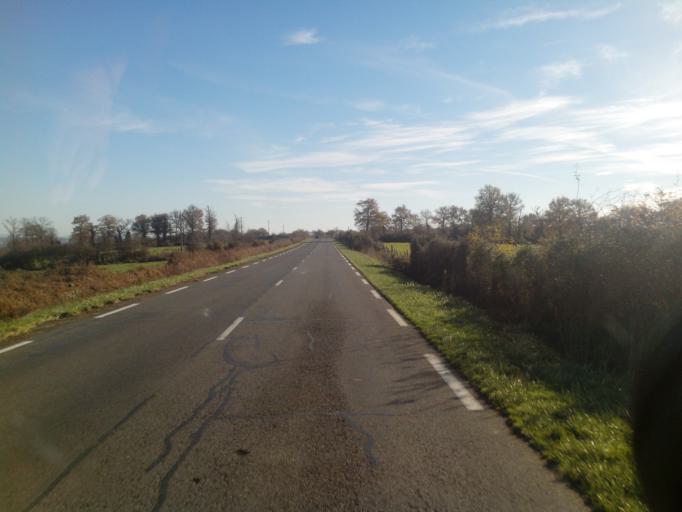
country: FR
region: Limousin
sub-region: Departement de la Haute-Vienne
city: Peyrat-de-Bellac
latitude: 46.1464
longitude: 0.9698
